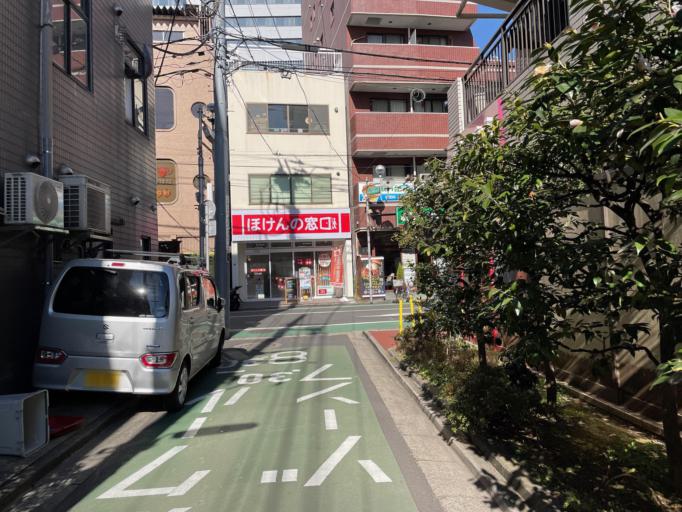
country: JP
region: Tokyo
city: Tokyo
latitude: 35.6067
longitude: 139.7041
